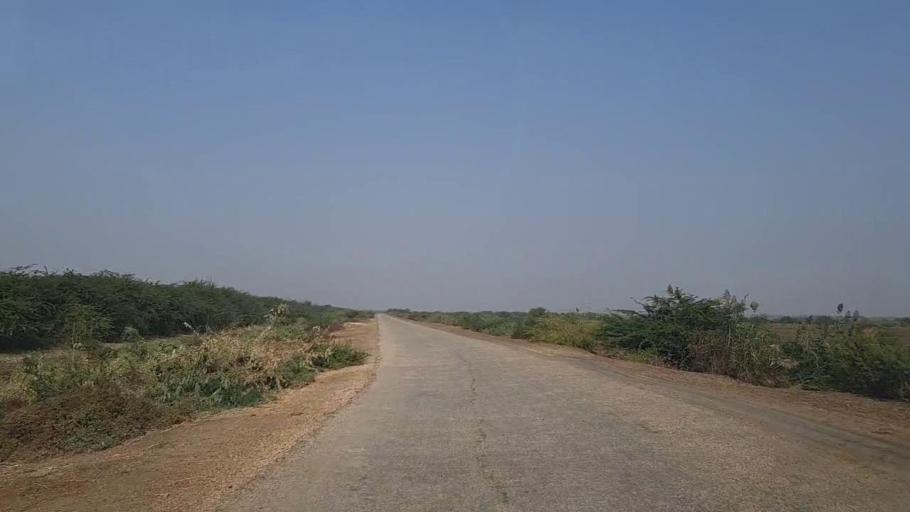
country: PK
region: Sindh
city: Keti Bandar
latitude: 24.2344
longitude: 67.6821
